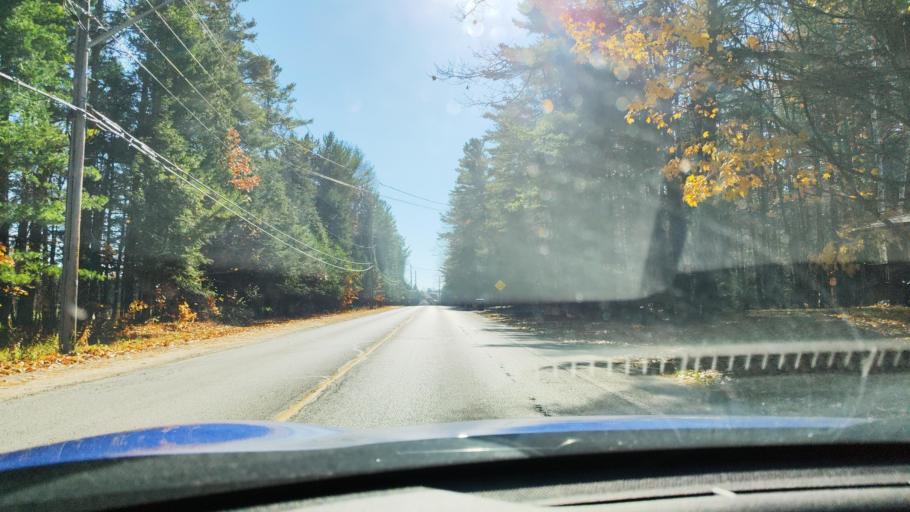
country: CA
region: Ontario
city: Wasaga Beach
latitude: 44.5151
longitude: -79.9951
